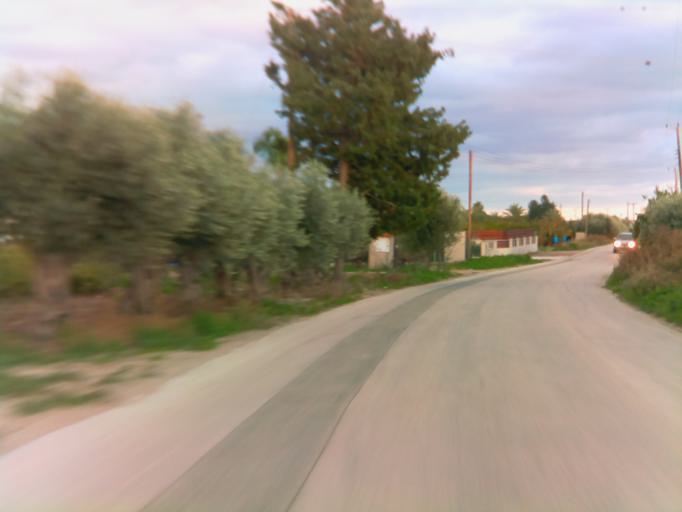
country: CY
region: Pafos
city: Pegeia
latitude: 34.8687
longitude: 32.3496
